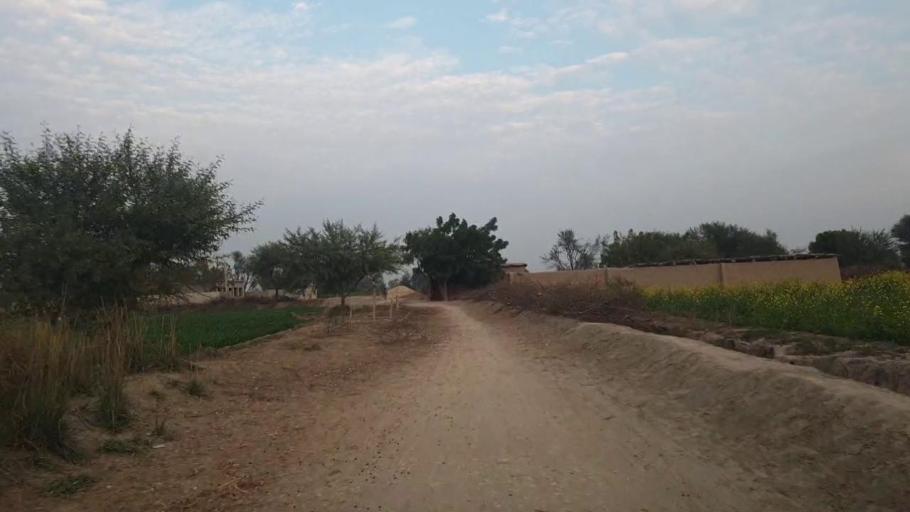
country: PK
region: Sindh
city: Shahpur Chakar
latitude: 26.0874
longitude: 68.5540
